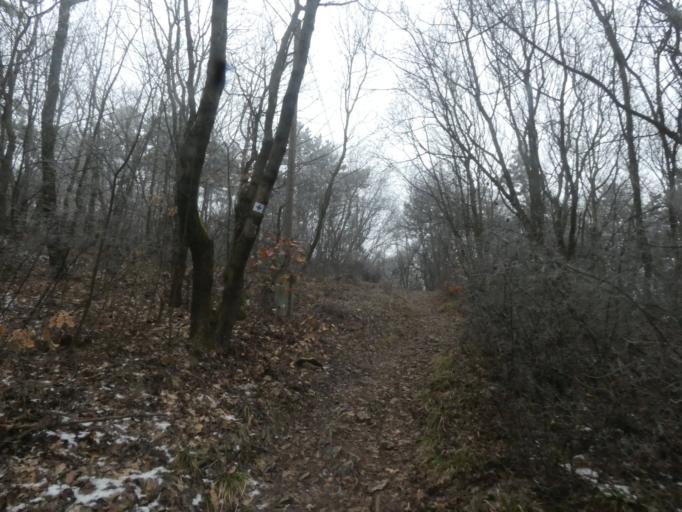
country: HU
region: Budapest
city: Budapest III. keruelet
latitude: 47.5411
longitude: 19.0146
